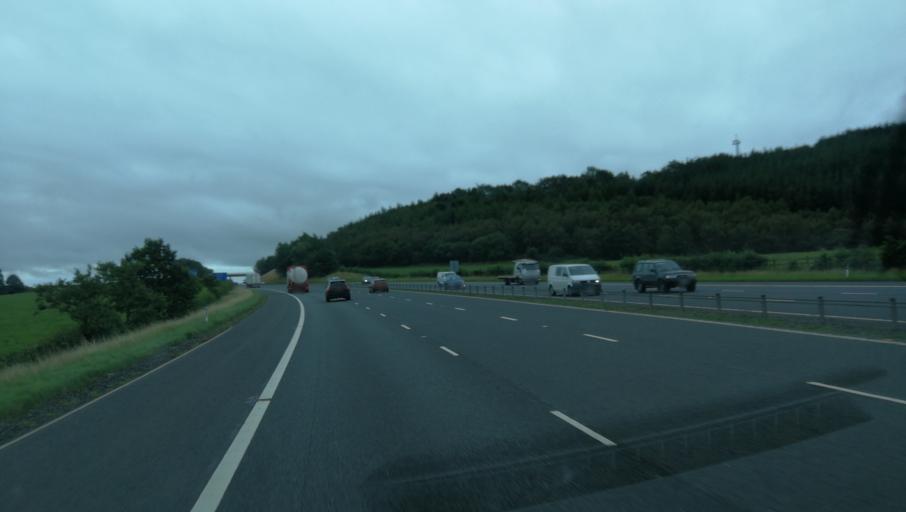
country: GB
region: Scotland
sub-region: Dumfries and Galloway
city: Annan
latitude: 55.0556
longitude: -3.2475
